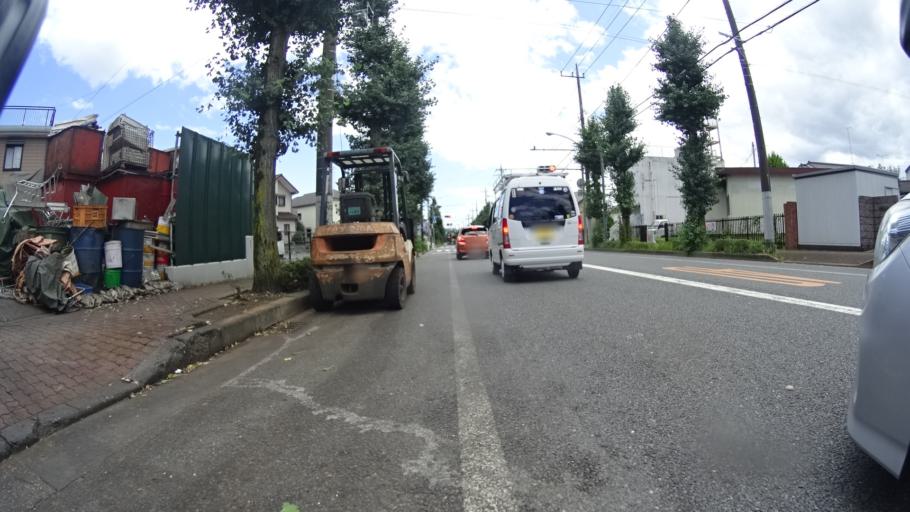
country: JP
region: Tokyo
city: Fussa
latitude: 35.7534
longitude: 139.3169
